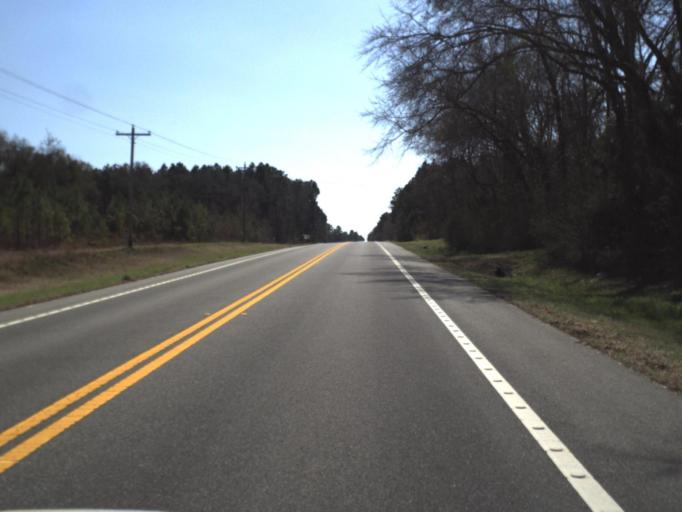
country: US
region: Florida
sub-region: Jackson County
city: Sneads
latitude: 30.6271
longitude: -85.0297
